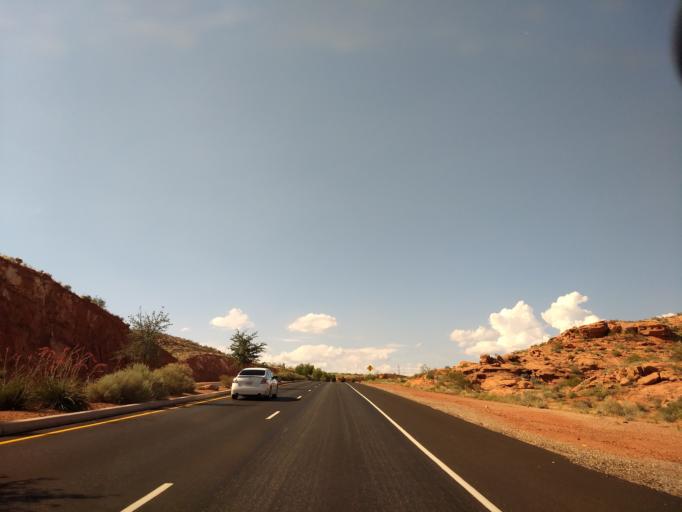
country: US
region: Utah
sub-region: Washington County
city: Saint George
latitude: 37.1216
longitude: -113.5837
